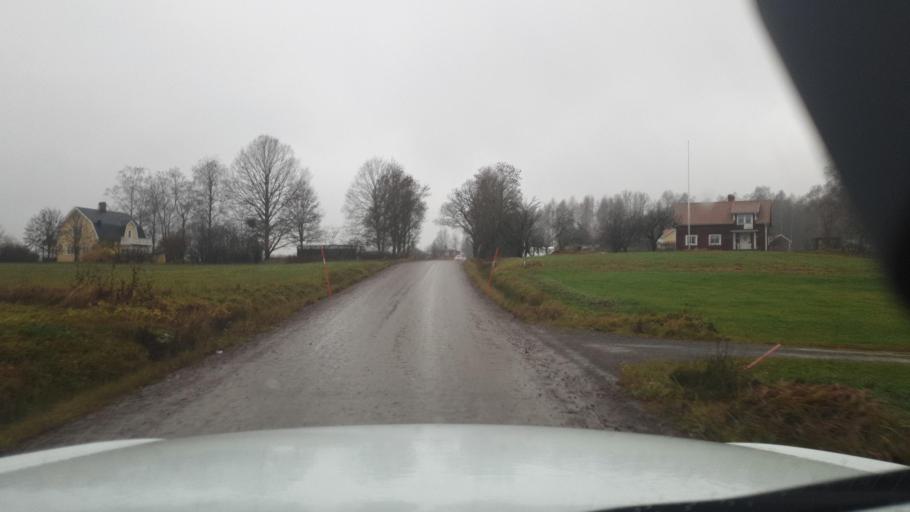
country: SE
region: Vaermland
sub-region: Sunne Kommun
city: Sunne
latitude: 59.7978
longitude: 13.1074
